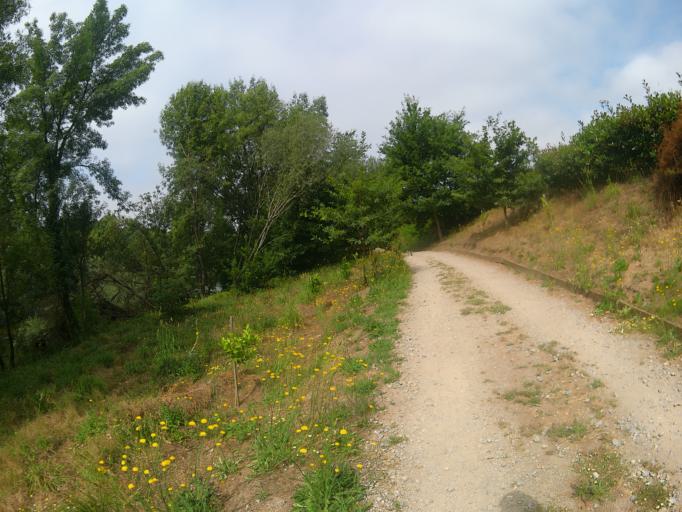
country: PT
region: Viana do Castelo
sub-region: Ponte de Lima
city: Ponte de Lima
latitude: 41.7841
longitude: -8.5269
